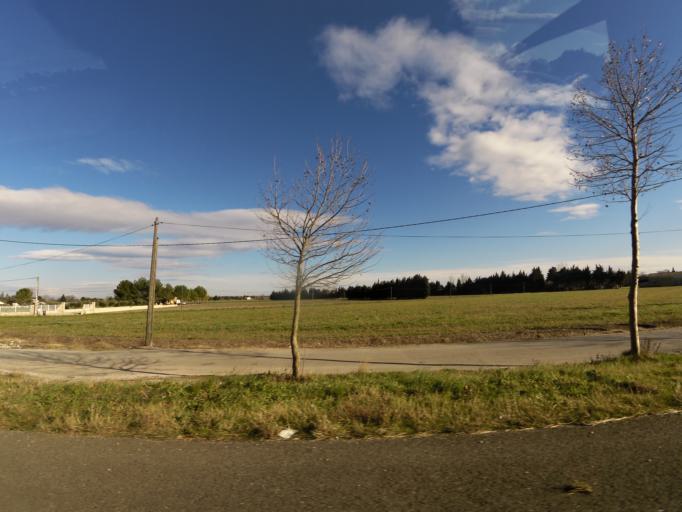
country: FR
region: Languedoc-Roussillon
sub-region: Departement du Gard
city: Uchaud
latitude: 43.7588
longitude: 4.2800
